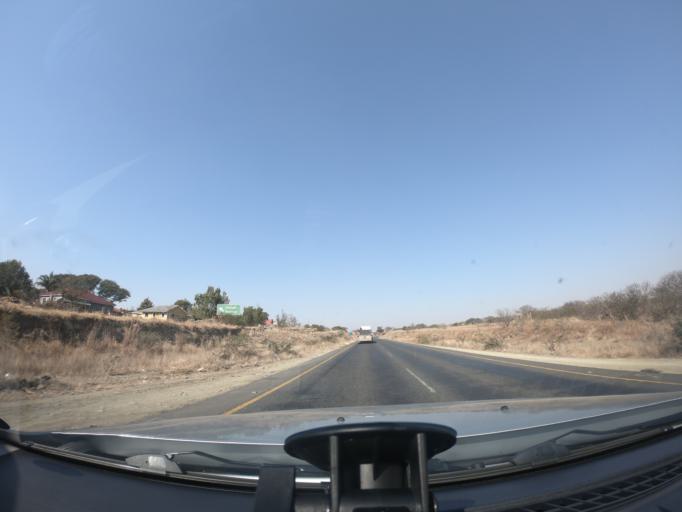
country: ZA
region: KwaZulu-Natal
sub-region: uThukela District Municipality
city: Ladysmith
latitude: -28.7465
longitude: 29.8207
